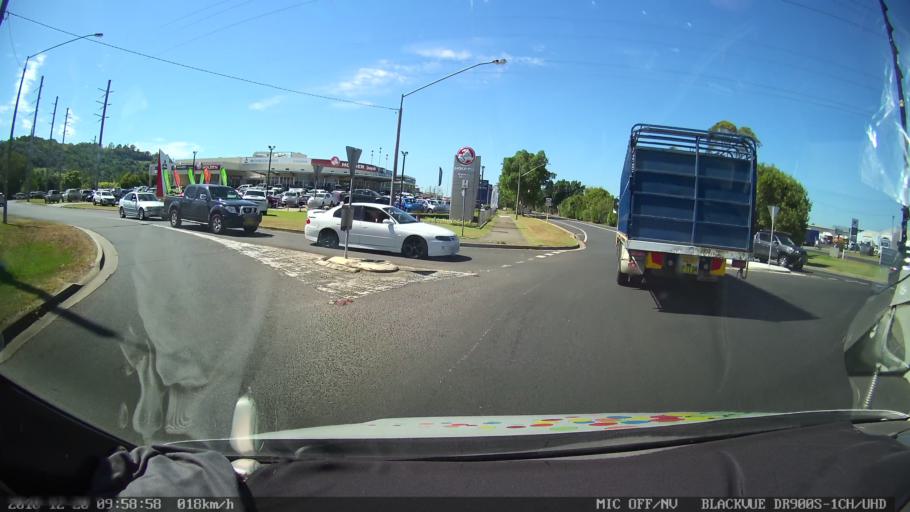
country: AU
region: New South Wales
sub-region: Lismore Municipality
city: Lismore
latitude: -28.8209
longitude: 153.2653
